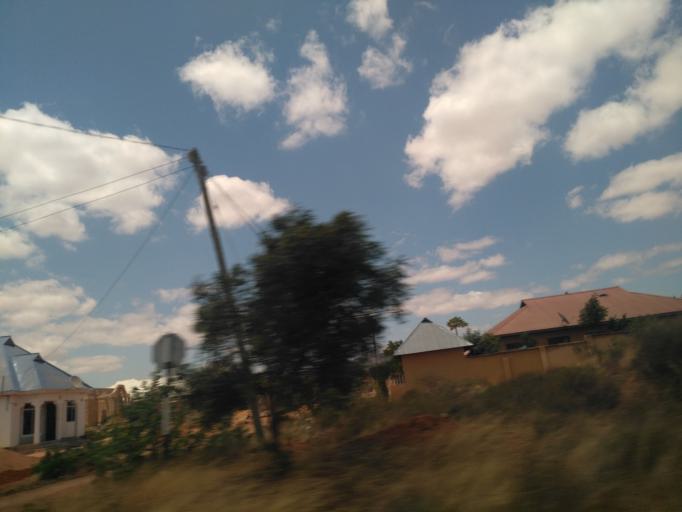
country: TZ
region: Dodoma
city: Kisasa
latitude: -6.1810
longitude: 35.7903
